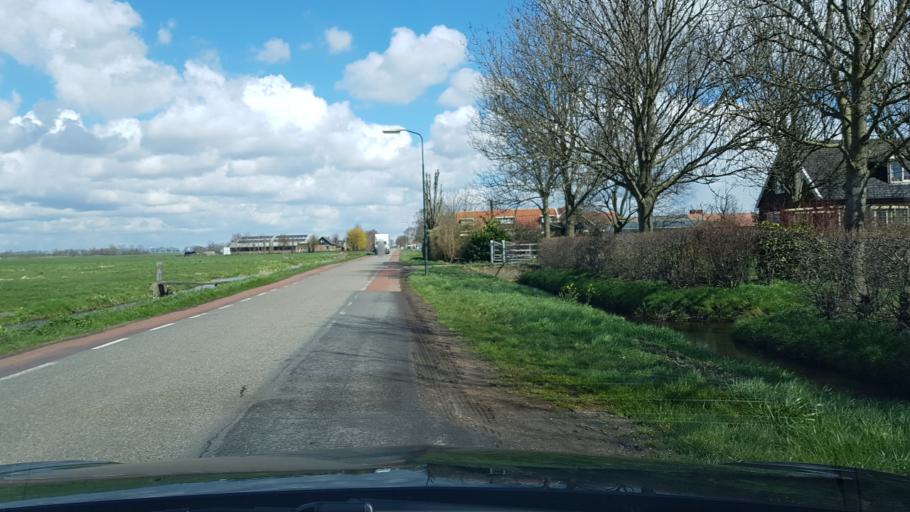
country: NL
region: Utrecht
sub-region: Gemeente De Ronde Venen
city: Mijdrecht
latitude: 52.2361
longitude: 4.8606
